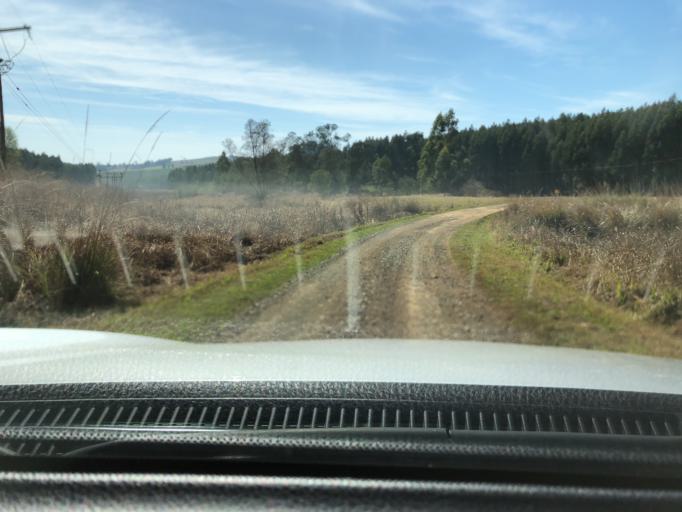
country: ZA
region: KwaZulu-Natal
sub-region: Sisonke District Municipality
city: Ixopo
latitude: -30.1814
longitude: 30.0476
